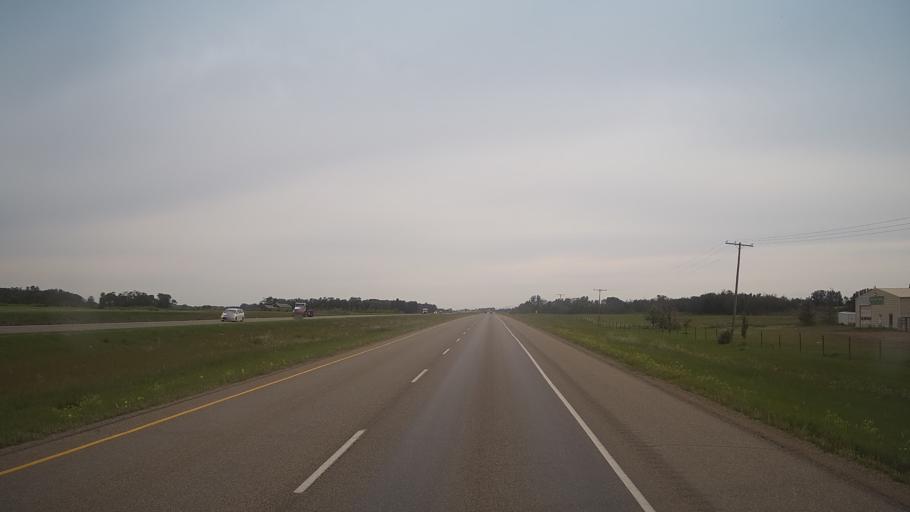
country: CA
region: Saskatchewan
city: Saskatoon
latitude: 52.0040
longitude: -106.5694
